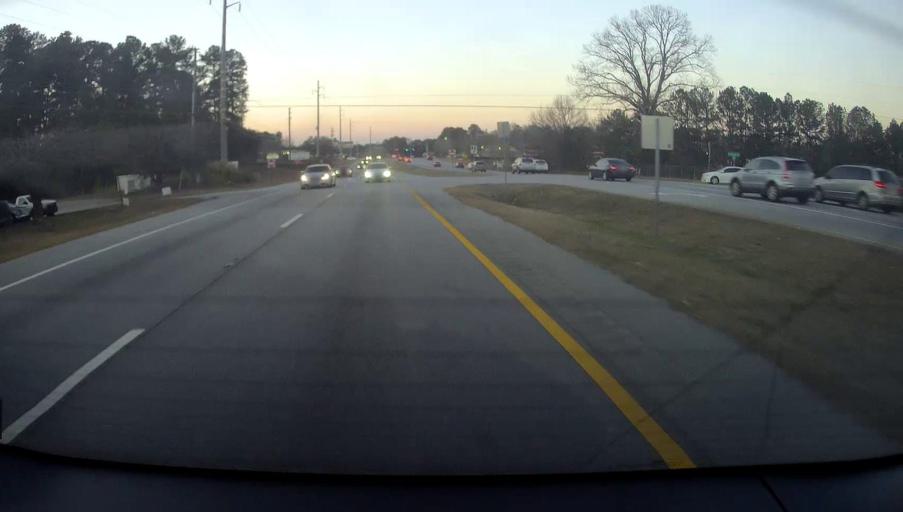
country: US
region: Georgia
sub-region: Fayette County
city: Fayetteville
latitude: 33.5061
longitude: -84.4286
